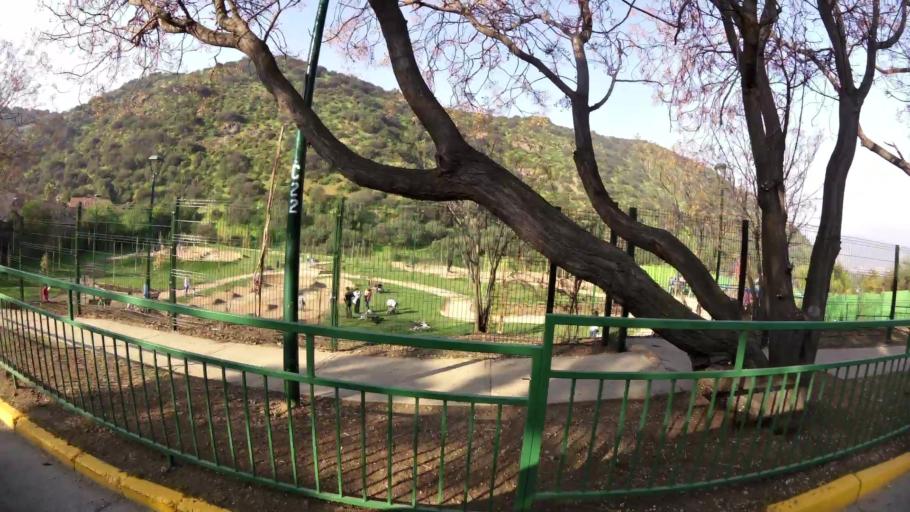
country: CL
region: Santiago Metropolitan
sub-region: Provincia de Santiago
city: Villa Presidente Frei, Nunoa, Santiago, Chile
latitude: -33.3469
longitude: -70.5397
